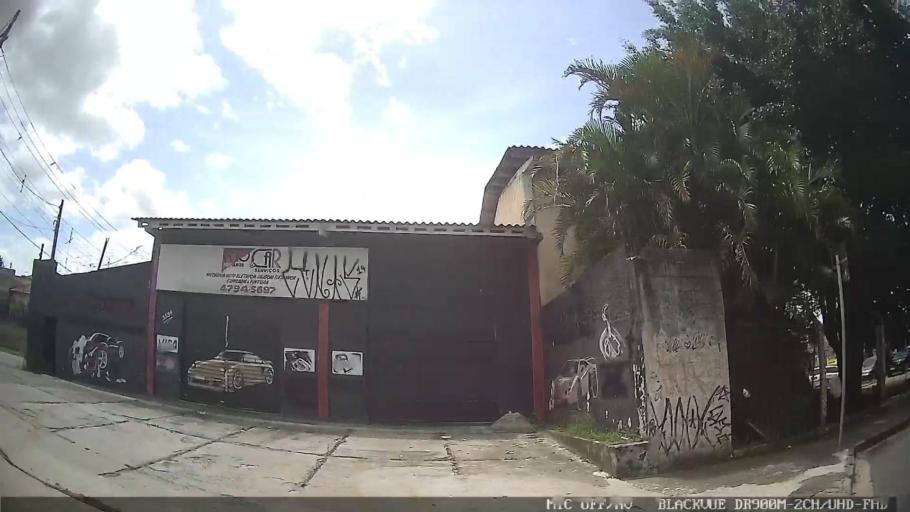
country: BR
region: Sao Paulo
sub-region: Mogi das Cruzes
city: Mogi das Cruzes
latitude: -23.5553
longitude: -46.2100
